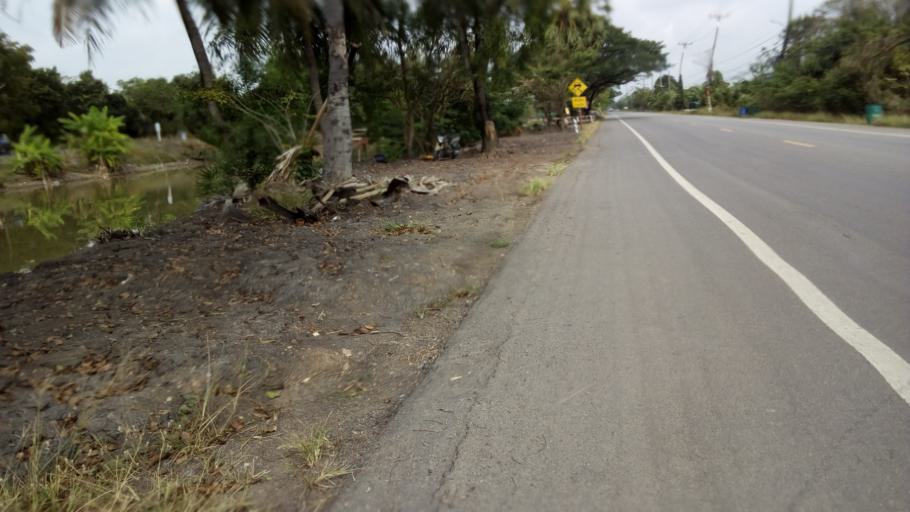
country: TH
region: Pathum Thani
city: Nong Suea
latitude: 14.1876
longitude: 100.8235
